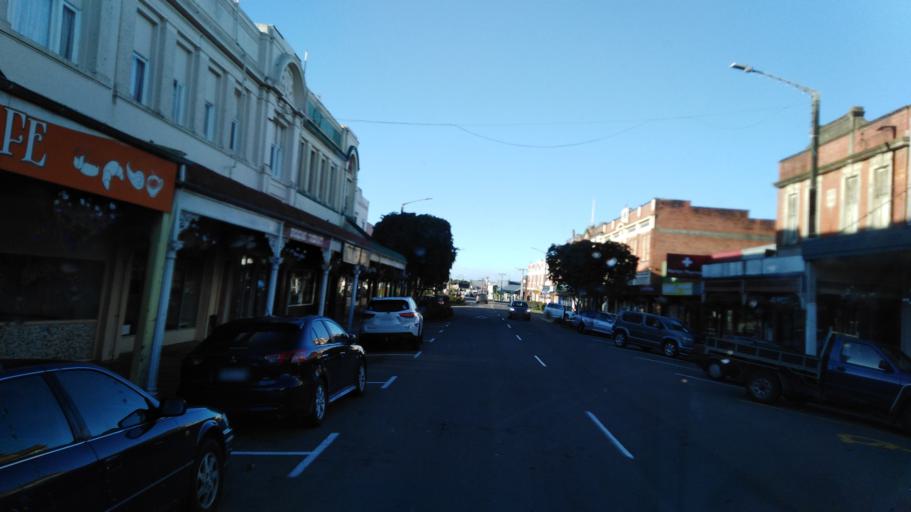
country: NZ
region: Manawatu-Wanganui
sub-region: Rangitikei District
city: Bulls
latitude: -40.0679
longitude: 175.3787
